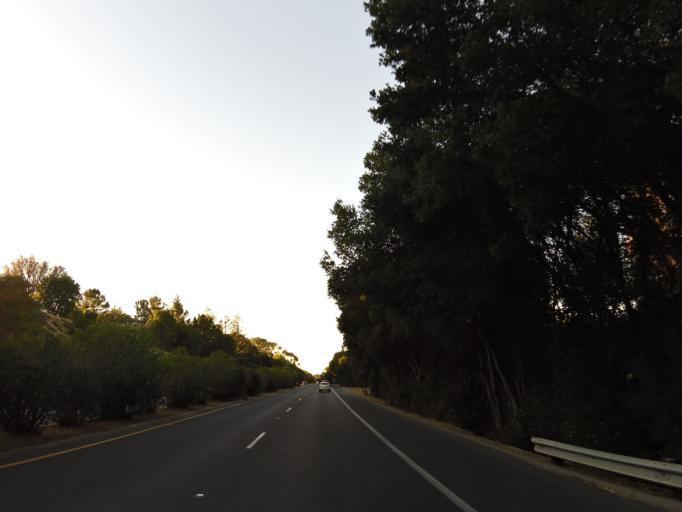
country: US
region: California
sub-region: Santa Clara County
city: Los Altos
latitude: 37.3883
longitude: -122.1268
